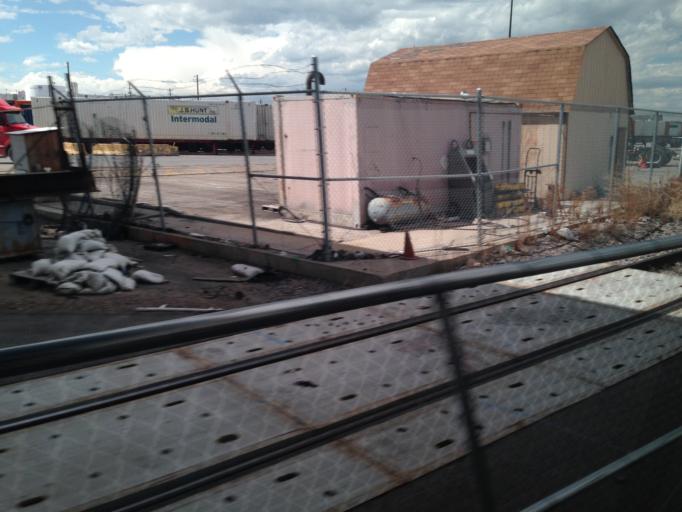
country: US
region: Colorado
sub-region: Adams County
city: Berkley
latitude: 39.7843
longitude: -104.9967
